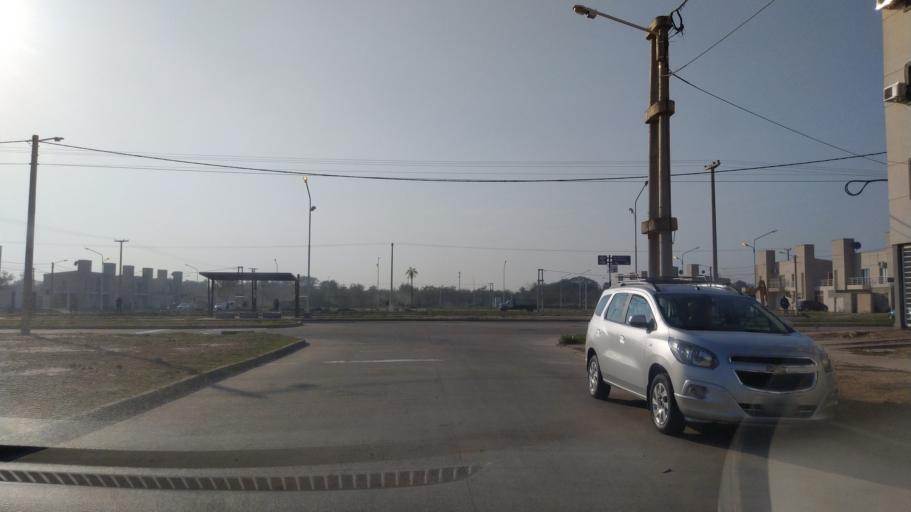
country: AR
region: Corrientes
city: Corrientes
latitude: -27.5263
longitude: -58.8041
